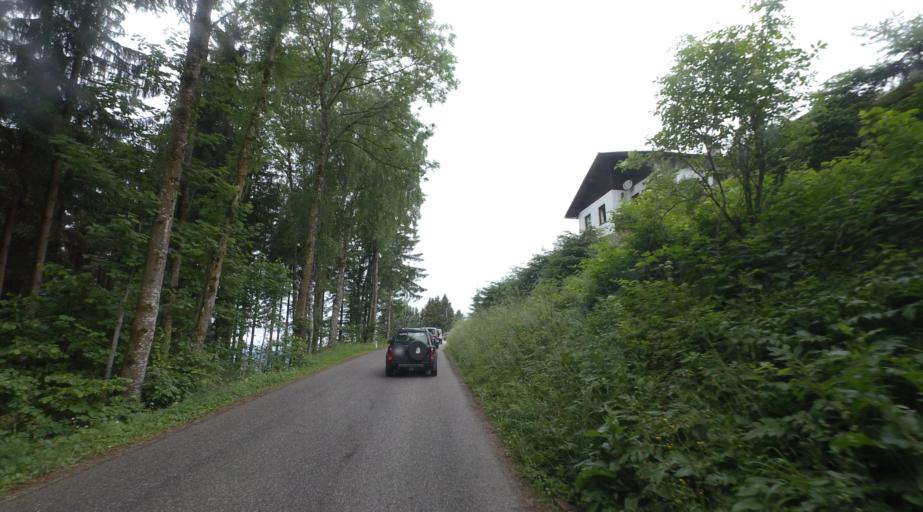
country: AT
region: Upper Austria
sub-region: Politischer Bezirk Kirchdorf an der Krems
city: Micheldorf in Oberoesterreich
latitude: 47.9342
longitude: 14.1730
